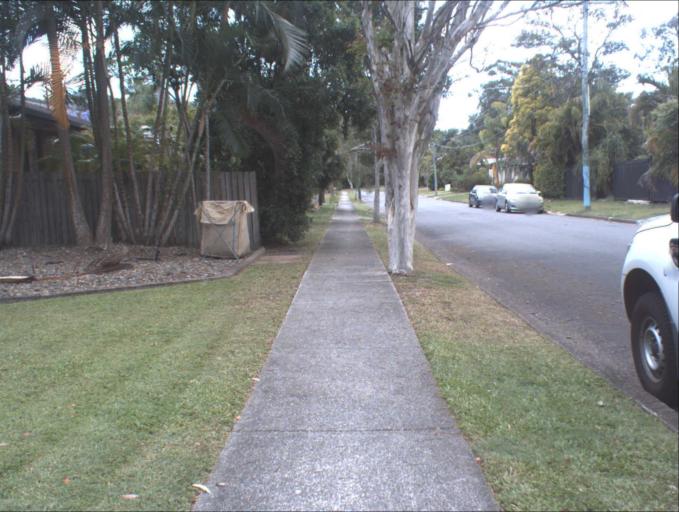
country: AU
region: Queensland
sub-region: Logan
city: Slacks Creek
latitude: -27.6418
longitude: 153.1684
